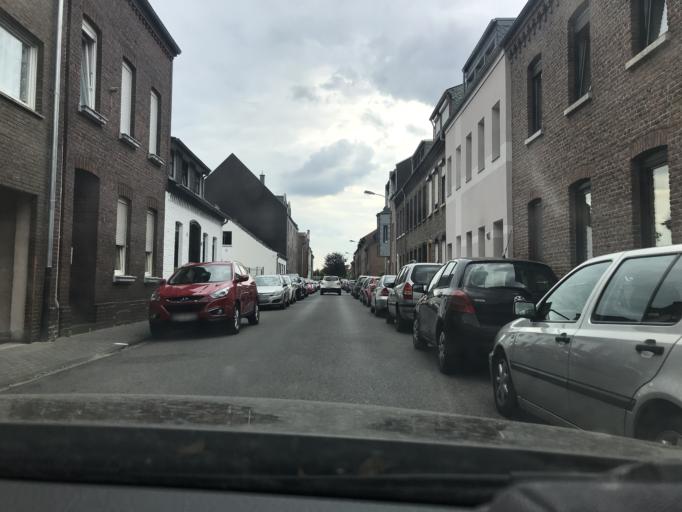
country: DE
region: North Rhine-Westphalia
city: Tonisvorst
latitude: 51.3242
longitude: 6.4878
